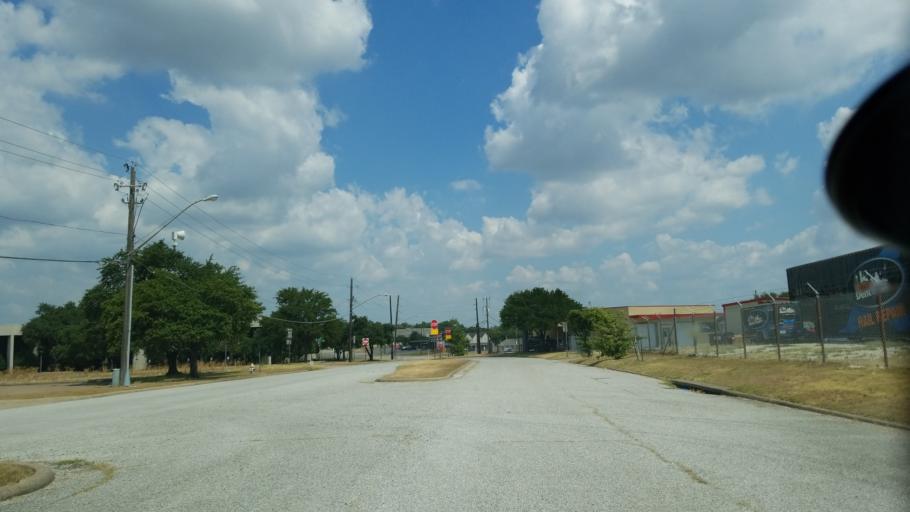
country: US
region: Texas
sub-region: Dallas County
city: Duncanville
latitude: 32.6920
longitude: -96.8935
